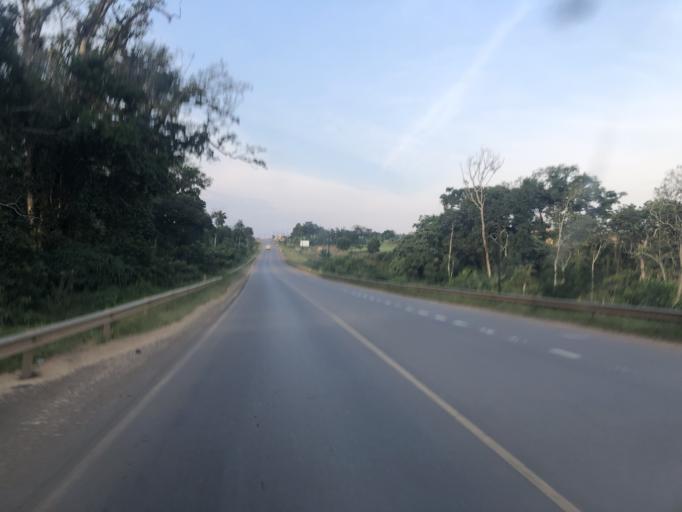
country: UG
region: Central Region
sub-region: Mpigi District
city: Mpigi
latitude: 0.2034
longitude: 32.3086
